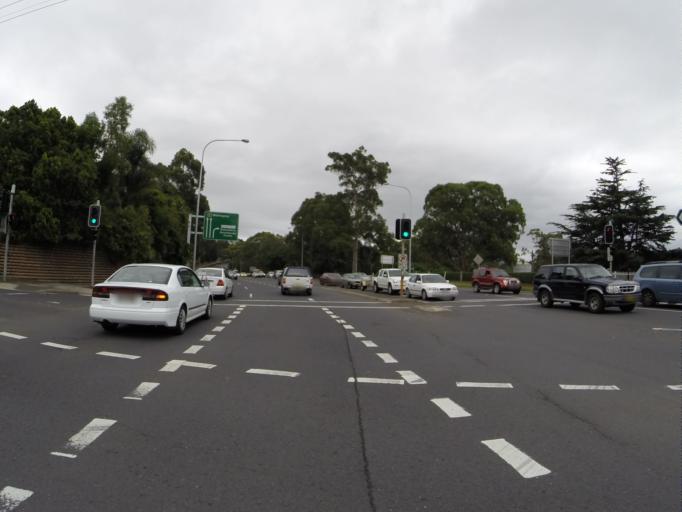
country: AU
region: New South Wales
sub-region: Shoalhaven Shire
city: Bomaderry
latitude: -34.8621
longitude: 150.6010
